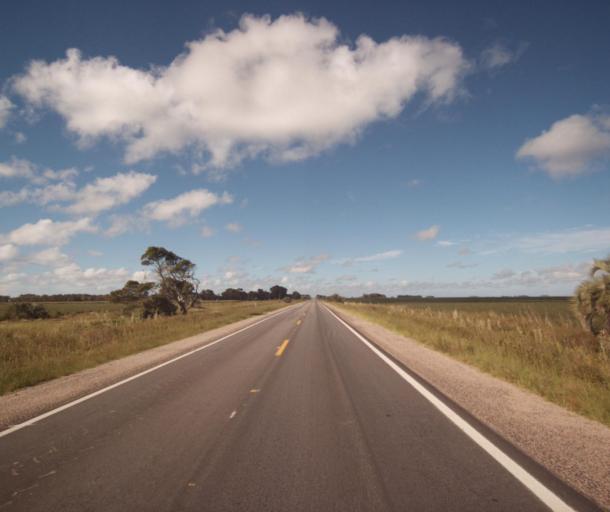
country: UY
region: Cerro Largo
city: Rio Branco
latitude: -32.9503
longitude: -52.7759
